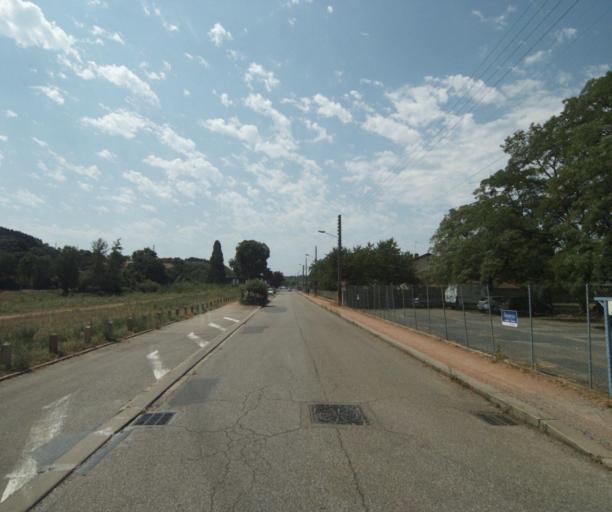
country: FR
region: Rhone-Alpes
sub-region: Departement du Rhone
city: Sain-Bel
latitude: 45.8290
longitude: 4.6124
